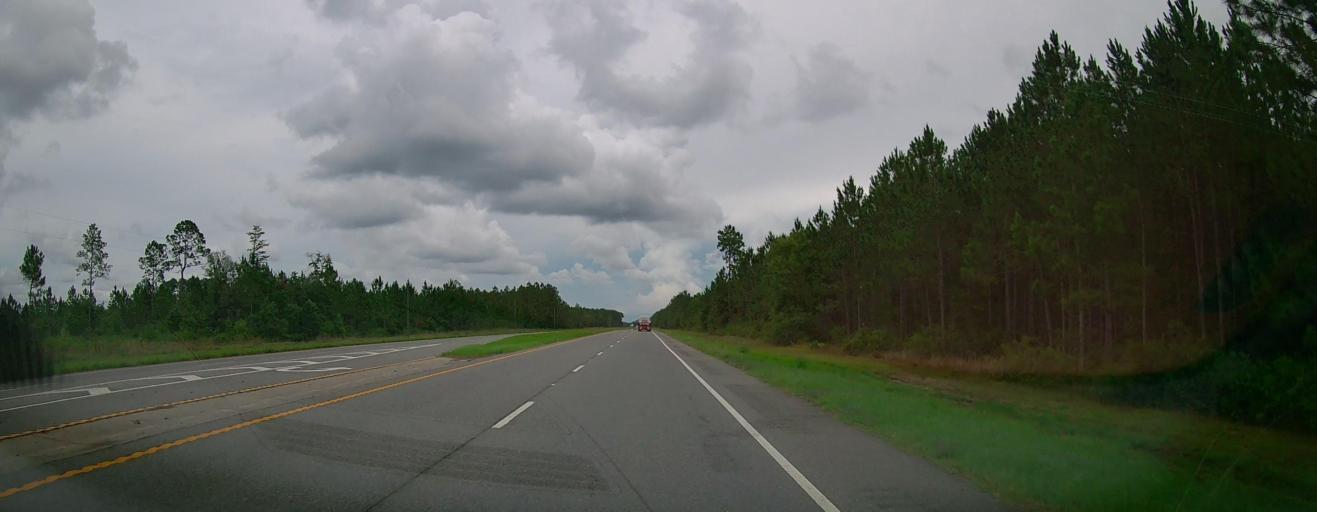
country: US
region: Georgia
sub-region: Wayne County
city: Jesup
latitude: 31.6740
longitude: -82.0687
